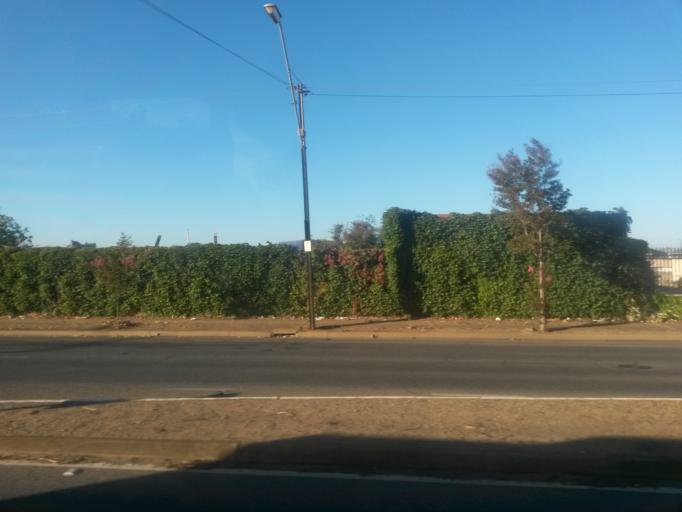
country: AU
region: South Australia
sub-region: Port Adelaide Enfield
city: Alberton
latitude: -34.8654
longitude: 138.5323
